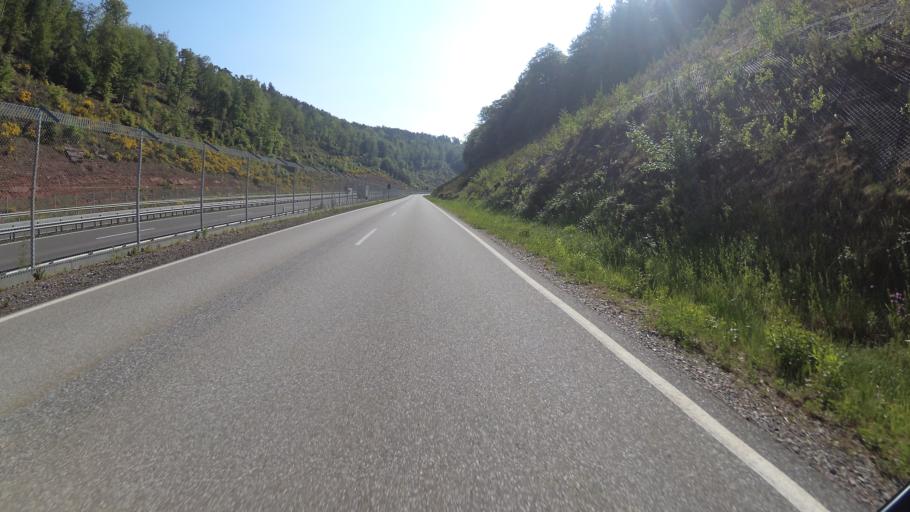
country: DE
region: Rheinland-Pfalz
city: Hinterweidenthal
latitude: 49.1976
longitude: 7.7265
